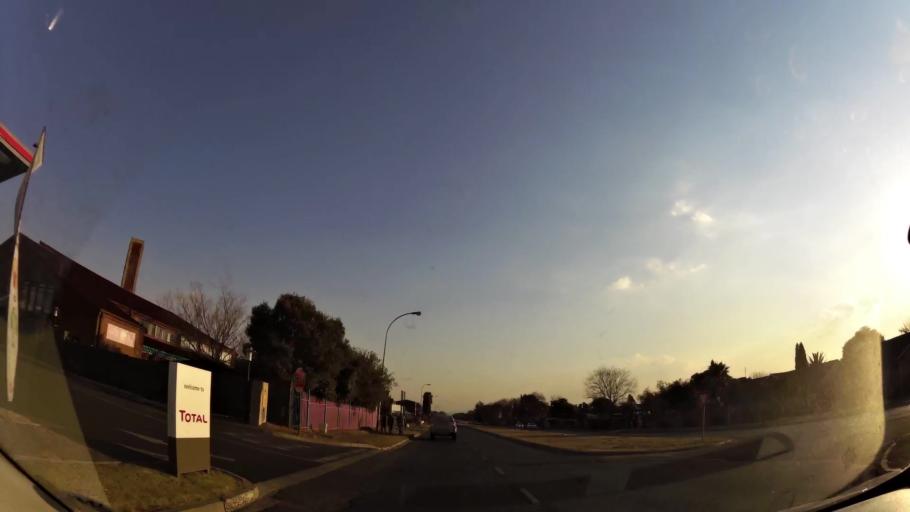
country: ZA
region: Gauteng
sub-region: Ekurhuleni Metropolitan Municipality
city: Germiston
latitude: -26.2663
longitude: 28.2274
